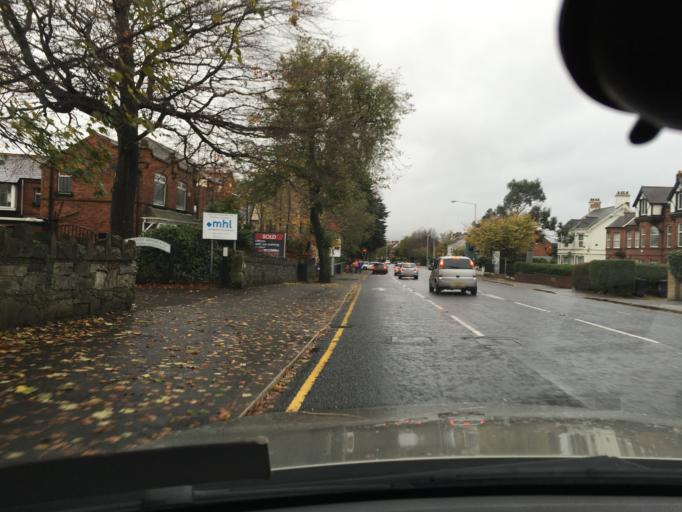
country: GB
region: Northern Ireland
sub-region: Castlereagh District
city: Castlereagh
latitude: 54.5956
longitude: -5.8736
